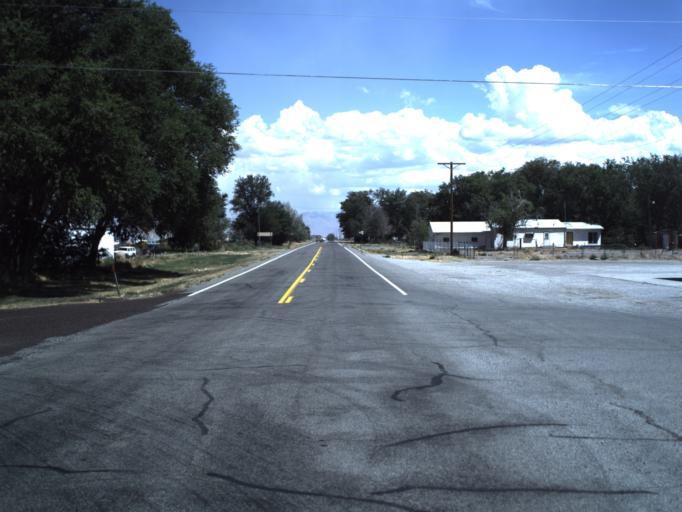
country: US
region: Utah
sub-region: Millard County
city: Delta
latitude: 39.3308
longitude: -112.6713
